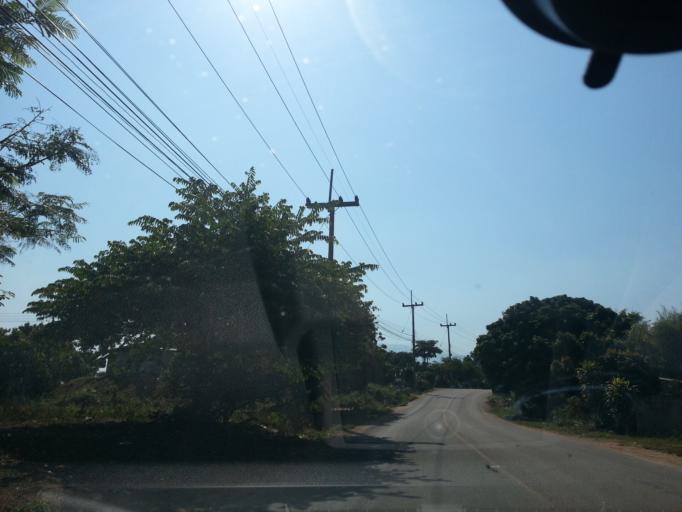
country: TH
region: Chiang Mai
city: Chai Prakan
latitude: 19.8165
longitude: 99.1076
